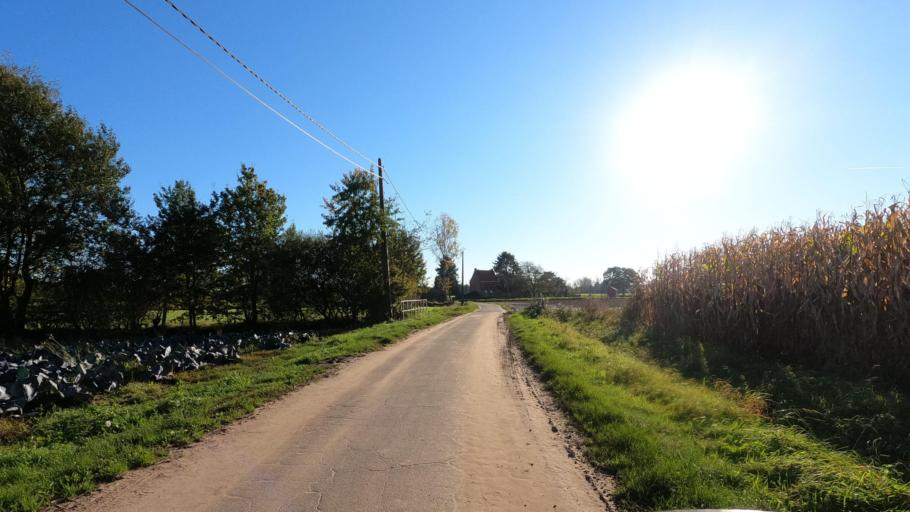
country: BE
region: Flanders
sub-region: Provincie Antwerpen
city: Herenthout
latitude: 51.1053
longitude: 4.7644
